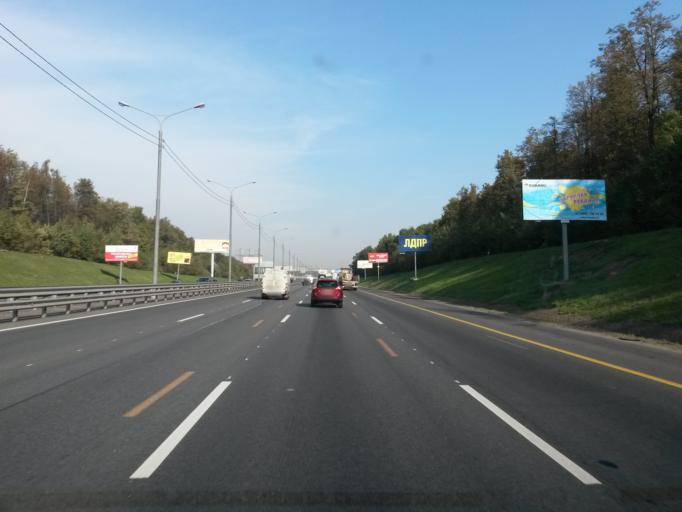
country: RU
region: Moscow
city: Annino
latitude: 55.5514
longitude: 37.6060
